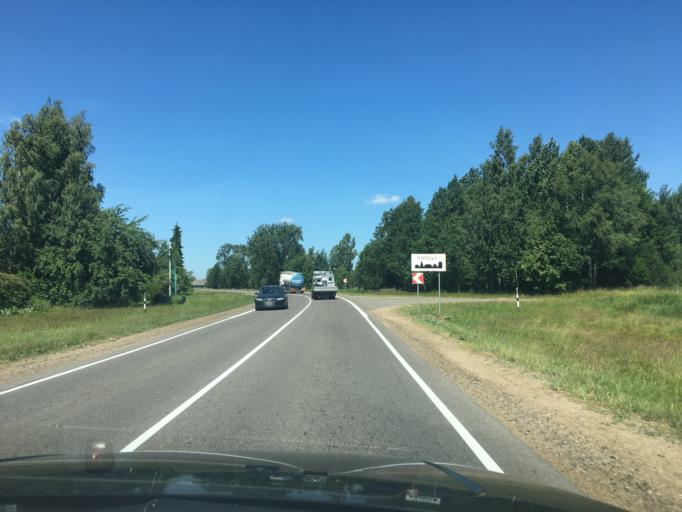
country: BY
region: Grodnenskaya
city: Iwye
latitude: 54.0571
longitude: 25.9145
